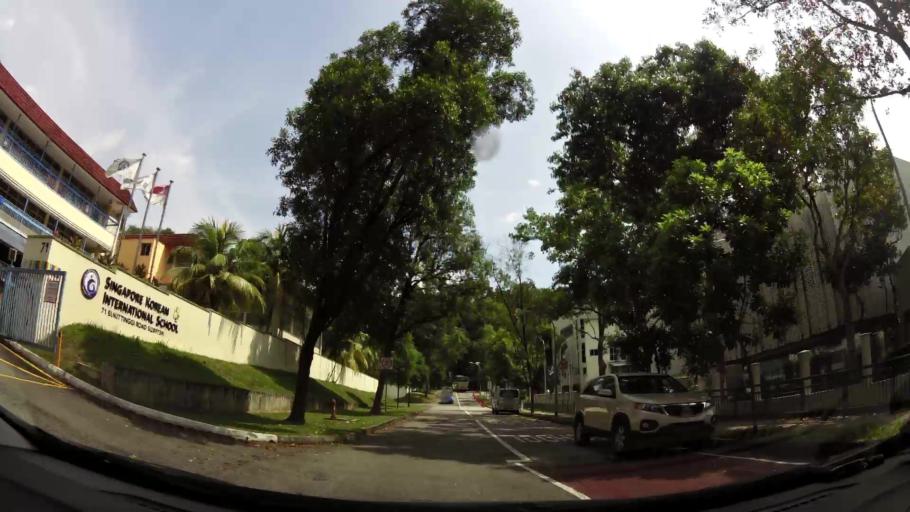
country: SG
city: Singapore
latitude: 1.3456
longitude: 103.7906
